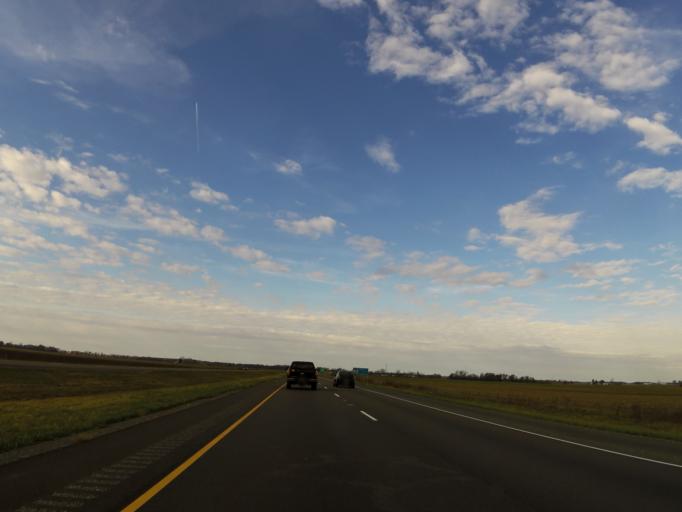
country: US
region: Illinois
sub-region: Washington County
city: Okawville
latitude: 38.4315
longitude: -89.5044
